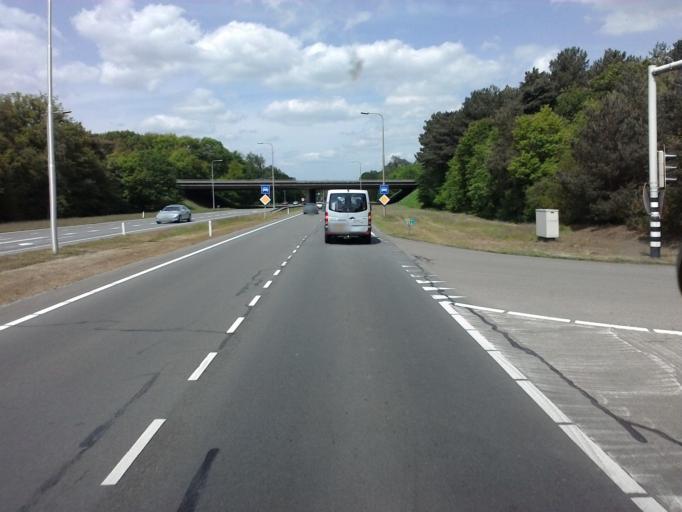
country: NL
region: Limburg
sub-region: Gemeente Gennep
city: Gennep
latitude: 51.6653
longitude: 5.9870
